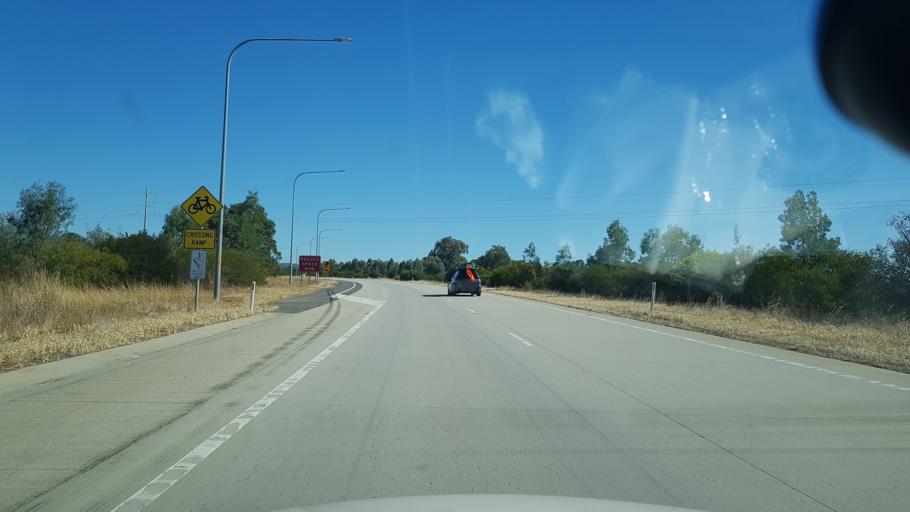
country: AU
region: New South Wales
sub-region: Greater Hume Shire
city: Jindera
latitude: -35.9271
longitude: 147.0068
